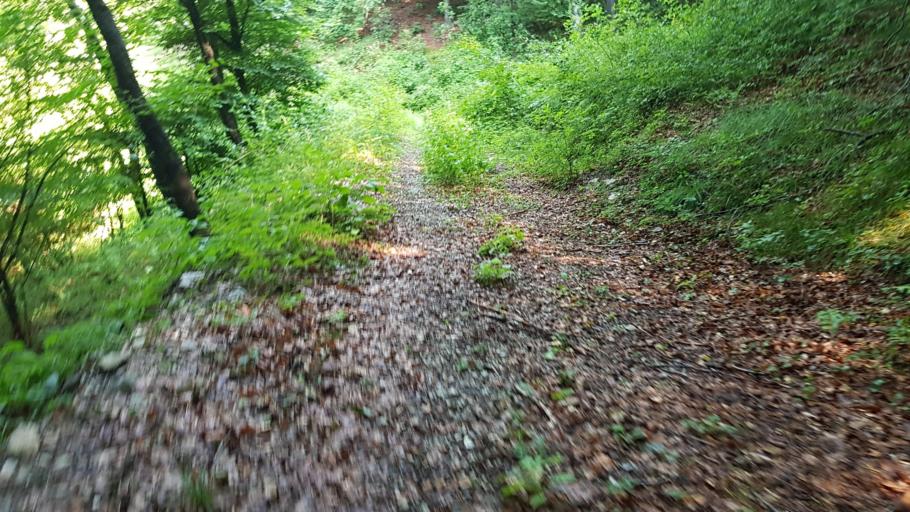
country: IT
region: Trentino-Alto Adige
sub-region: Provincia di Trento
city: Lasino
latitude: 46.0129
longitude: 10.9956
